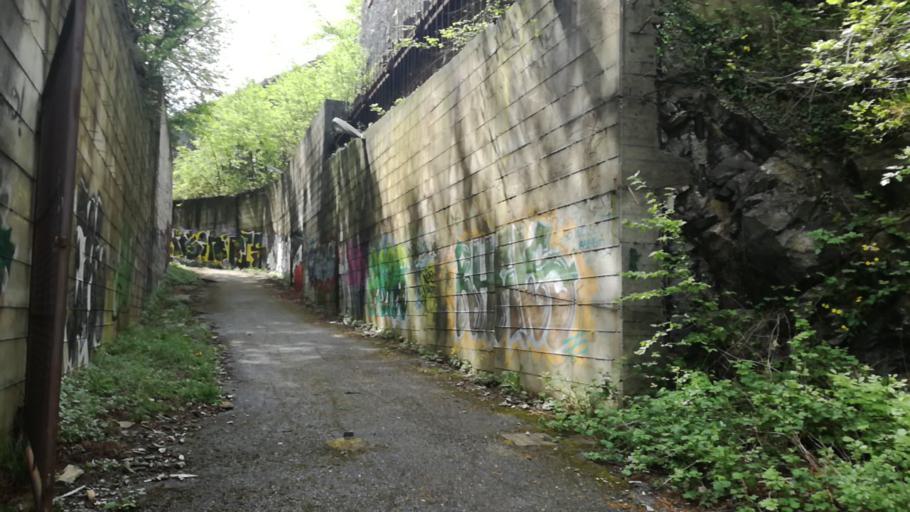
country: IT
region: Liguria
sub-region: Provincia di Genova
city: Genoa
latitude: 44.4391
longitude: 8.9226
